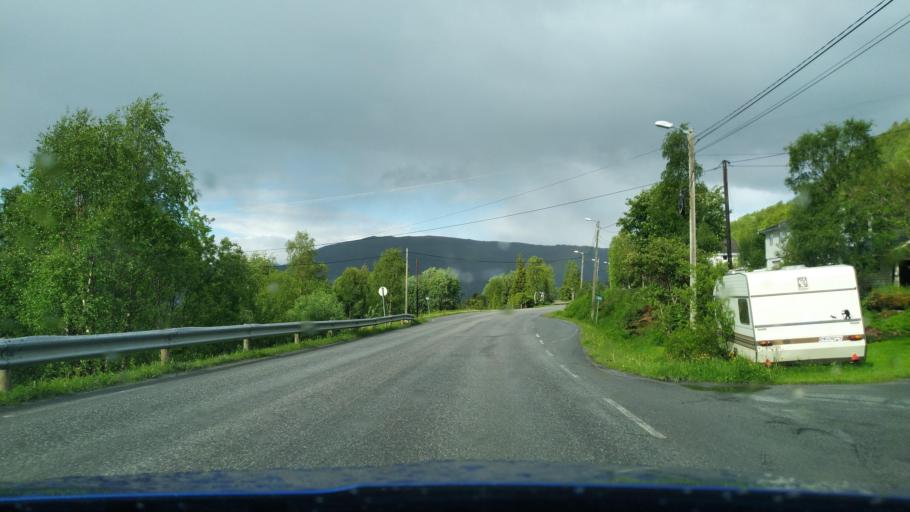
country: NO
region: Troms
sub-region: Sorreisa
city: Sorreisa
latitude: 69.1354
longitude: 18.0865
